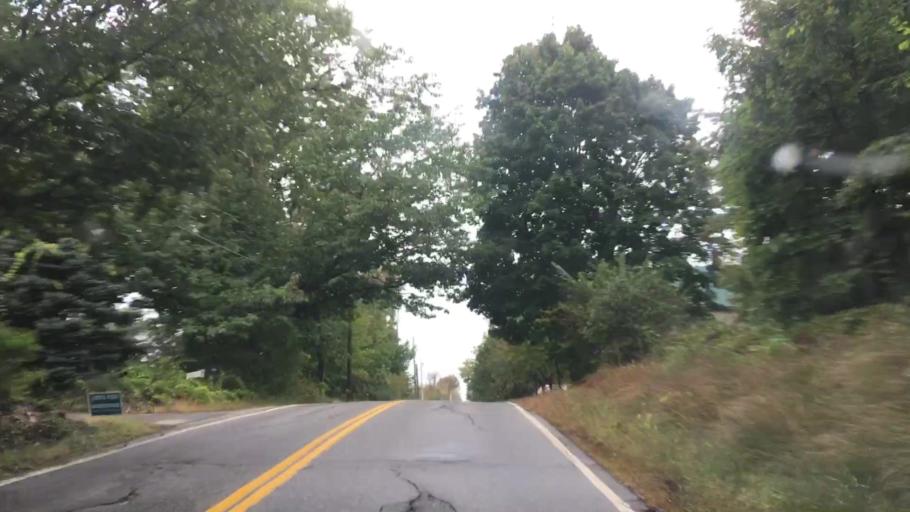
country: US
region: Maine
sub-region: Cumberland County
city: Raymond
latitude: 43.9766
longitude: -70.4705
